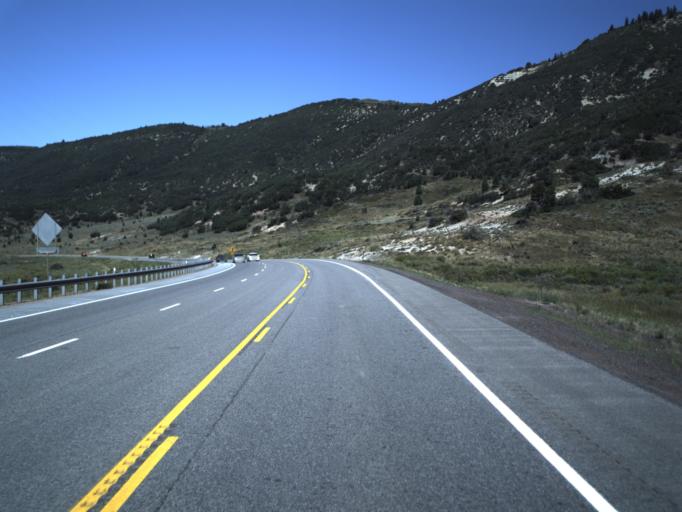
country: US
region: Utah
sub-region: Carbon County
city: Helper
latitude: 39.9302
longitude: -111.0863
